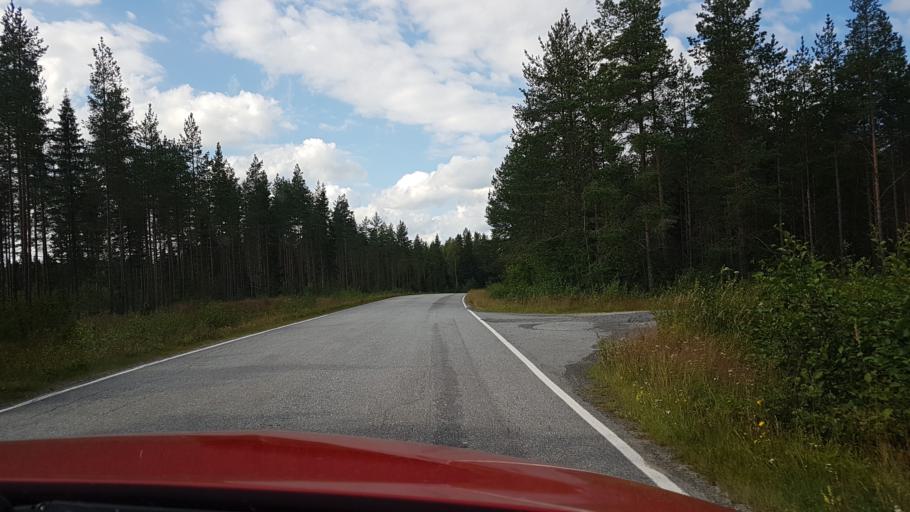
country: FI
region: Northern Ostrobothnia
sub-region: Ylivieska
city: Himanka
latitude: 64.0772
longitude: 23.7142
